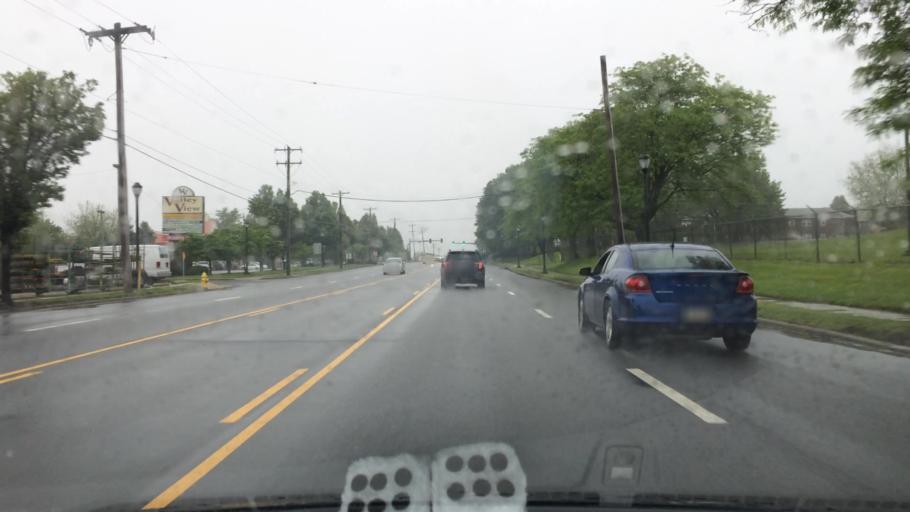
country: US
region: Pennsylvania
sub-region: Delaware County
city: Village Green-Green Ridge
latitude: 39.8628
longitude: -75.4277
